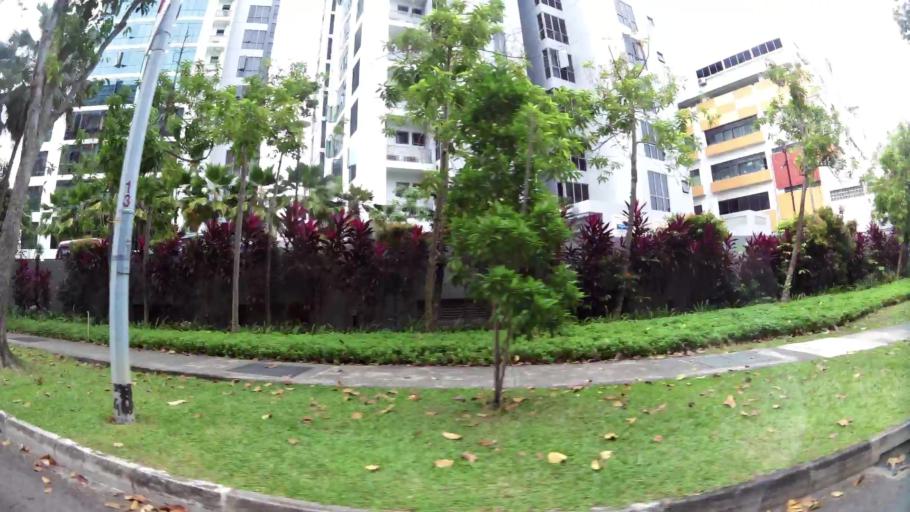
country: SG
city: Singapore
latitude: 1.3529
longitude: 103.8786
